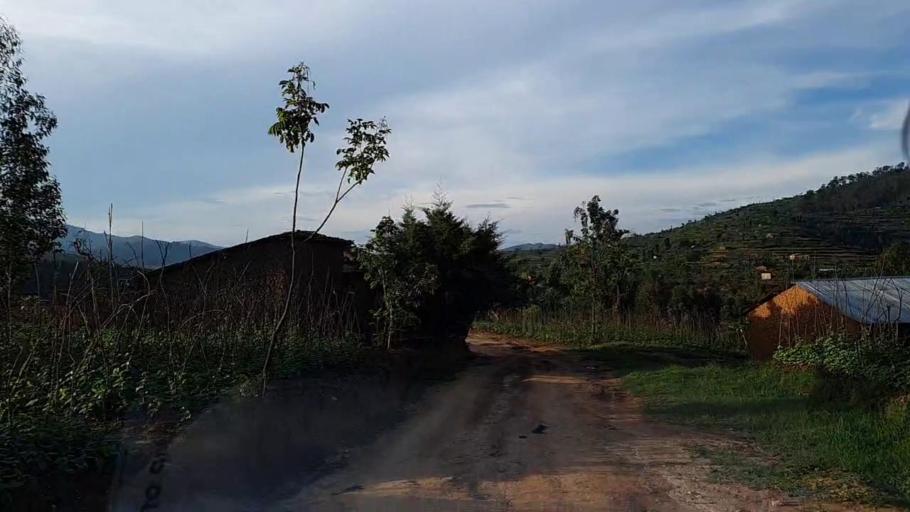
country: RW
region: Southern Province
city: Gikongoro
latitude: -2.4014
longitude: 29.5554
